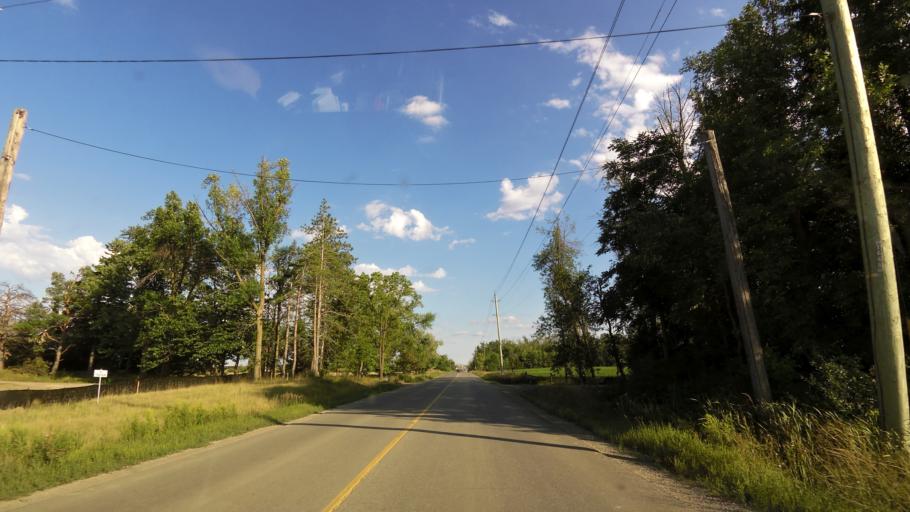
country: CA
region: Ontario
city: Brampton
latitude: 43.7119
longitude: -79.8432
